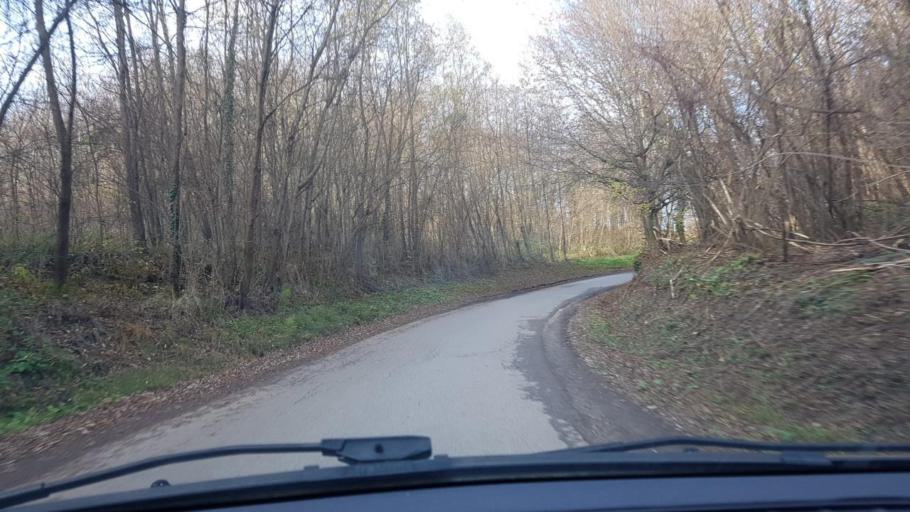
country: HR
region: Krapinsko-Zagorska
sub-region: Grad Krapina
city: Krapina
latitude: 46.1318
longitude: 15.8717
